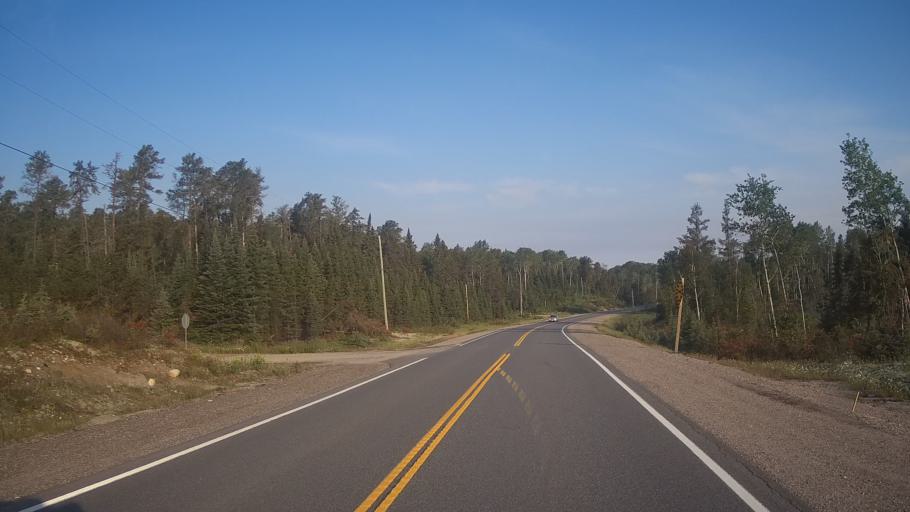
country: CA
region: Ontario
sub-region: Rainy River District
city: Atikokan
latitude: 49.3506
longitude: -91.5176
